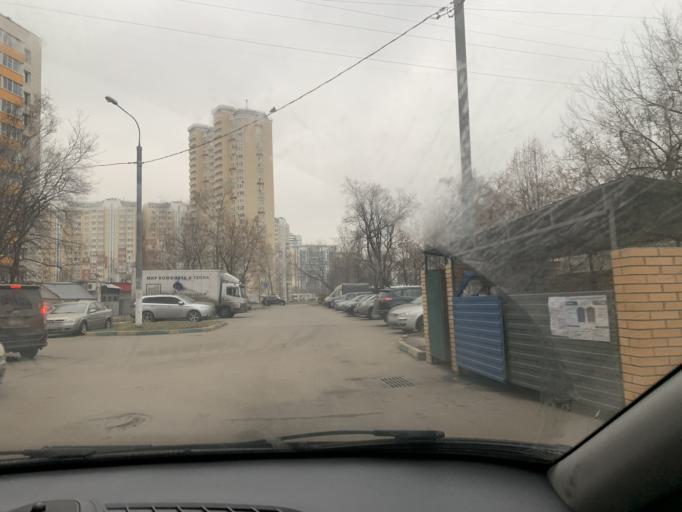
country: RU
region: Moskovskaya
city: Vostochnoe Degunino
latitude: 55.8748
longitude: 37.5486
